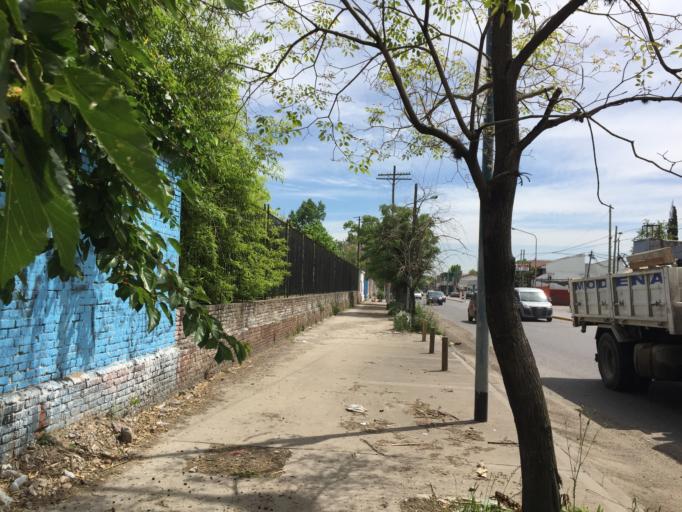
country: AR
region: Buenos Aires
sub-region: Partido de Lanus
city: Lanus
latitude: -34.7325
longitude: -58.3902
